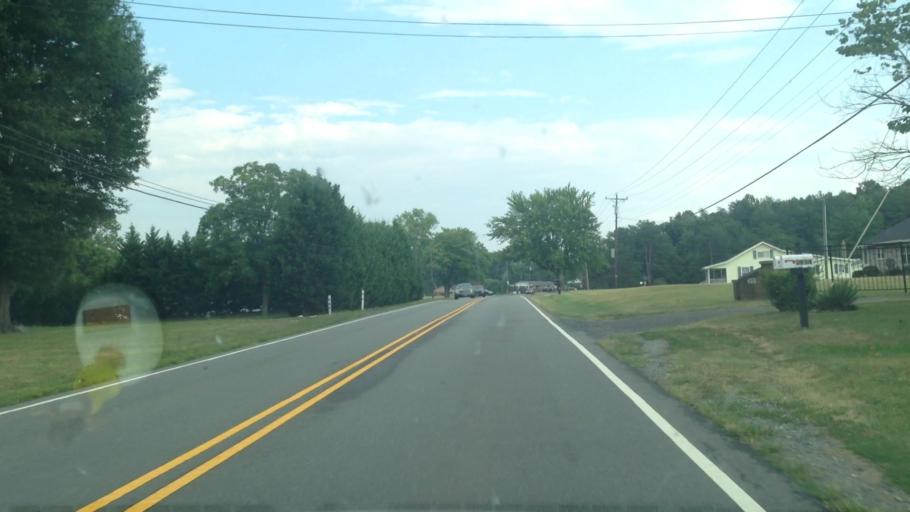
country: US
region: North Carolina
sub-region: Forsyth County
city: Walkertown
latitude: 36.1540
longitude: -80.1288
